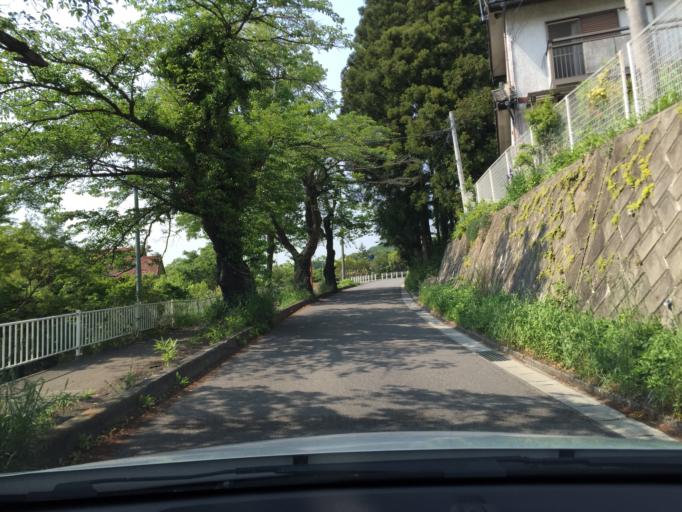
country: JP
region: Tochigi
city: Kuroiso
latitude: 37.1162
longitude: 140.2098
